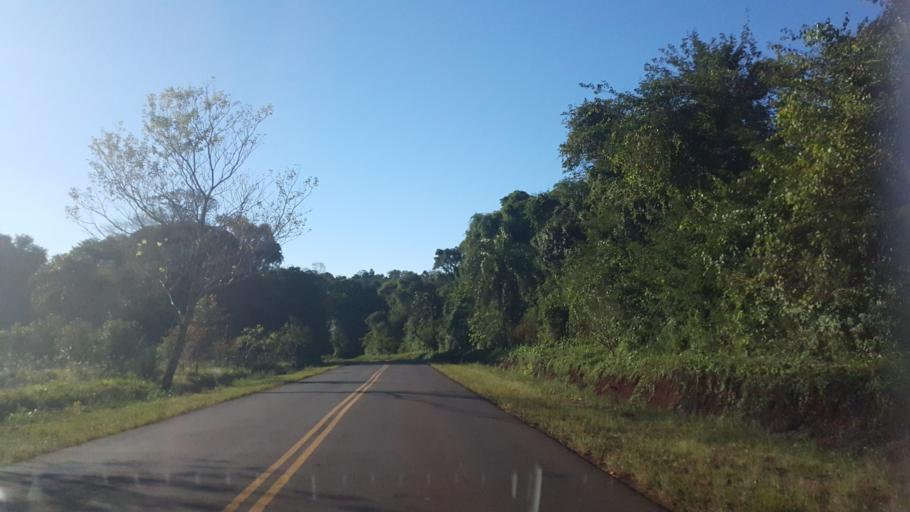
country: AR
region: Misiones
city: Capiovi
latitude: -26.9583
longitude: -55.0923
